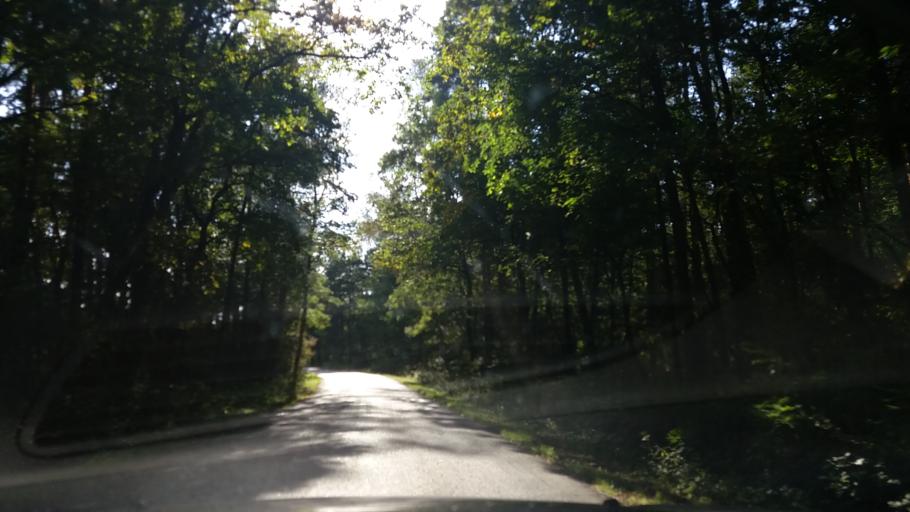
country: PL
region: Lesser Poland Voivodeship
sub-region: Powiat chrzanowski
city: Alwernia
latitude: 50.0443
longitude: 19.5478
